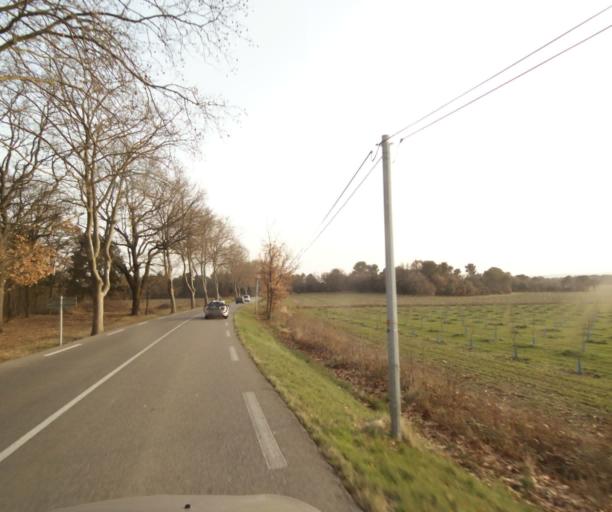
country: FR
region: Provence-Alpes-Cote d'Azur
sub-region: Departement des Bouches-du-Rhone
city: Eguilles
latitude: 43.6104
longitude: 5.3653
